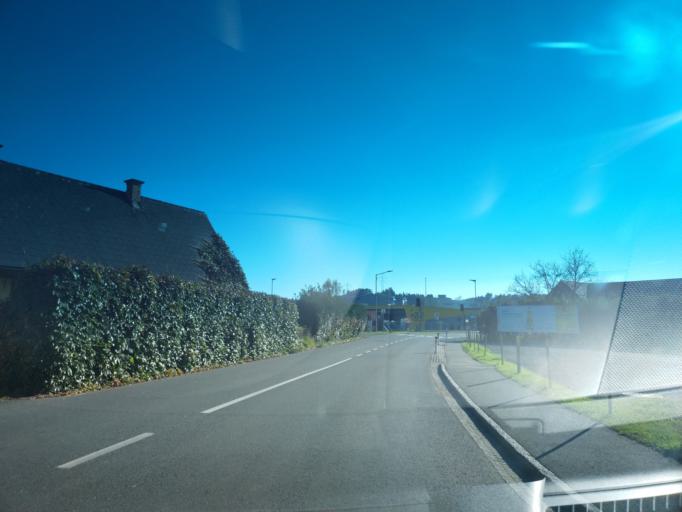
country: AT
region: Styria
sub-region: Politischer Bezirk Deutschlandsberg
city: Gross Sankt Florian
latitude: 46.8209
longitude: 15.3165
